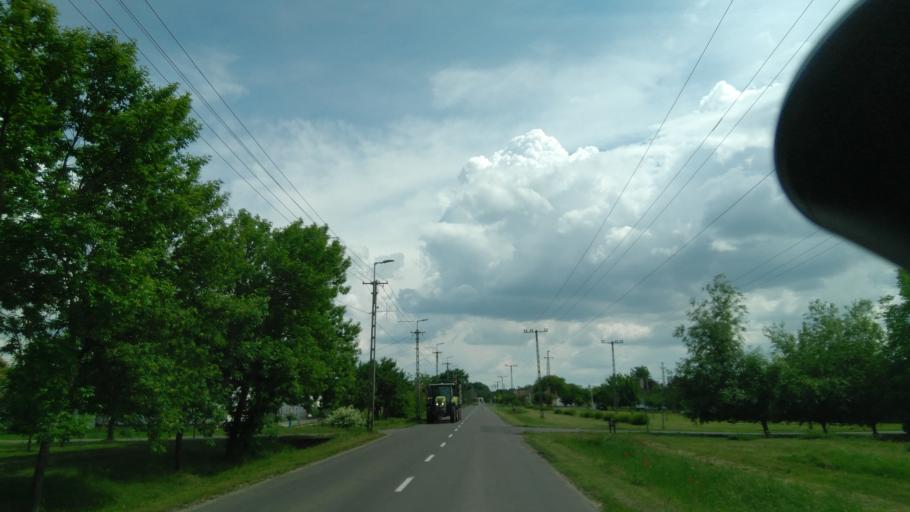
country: HU
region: Bekes
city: Mezohegyes
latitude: 46.3277
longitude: 20.8116
